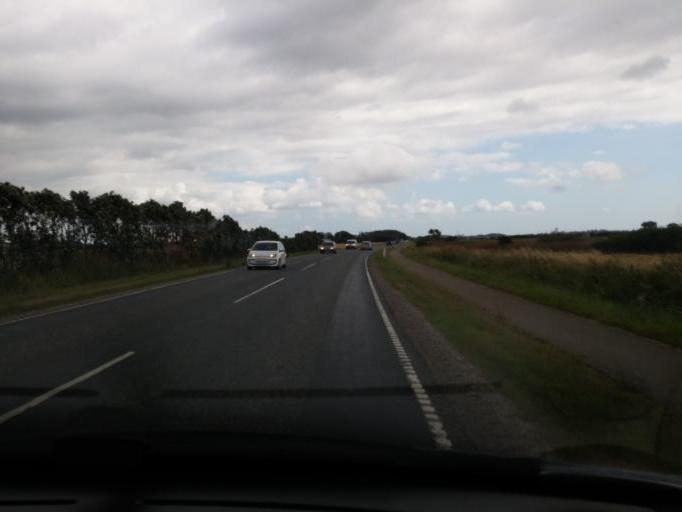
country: DK
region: South Denmark
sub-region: Langeland Kommune
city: Rudkobing
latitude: 54.9581
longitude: 10.6770
